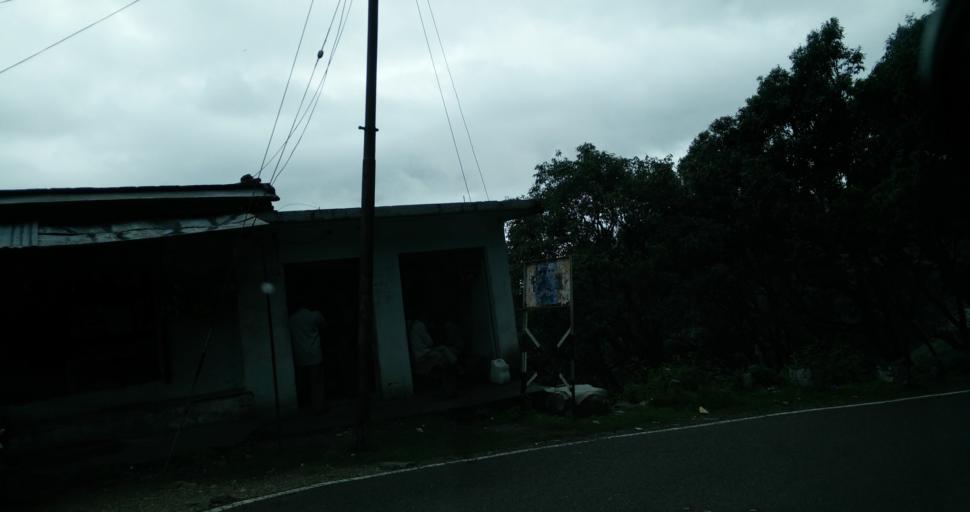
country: IN
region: Uttarakhand
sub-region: Garhwal
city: Lansdowne
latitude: 29.8610
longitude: 78.6802
